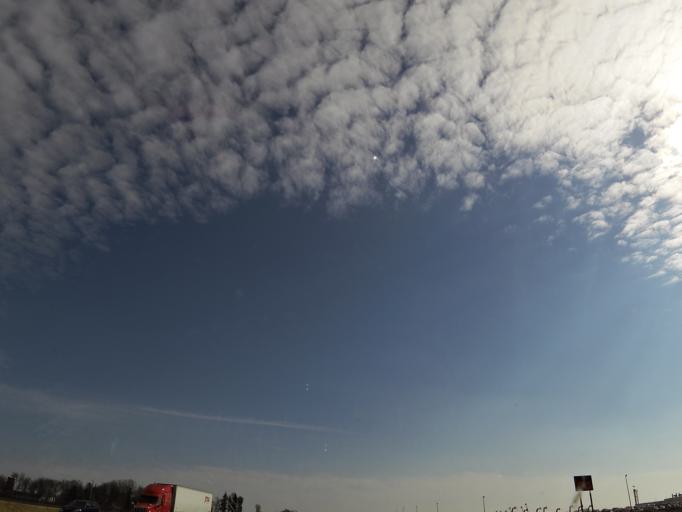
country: US
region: Minnesota
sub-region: Steele County
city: Medford
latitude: 44.1602
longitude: -93.2576
